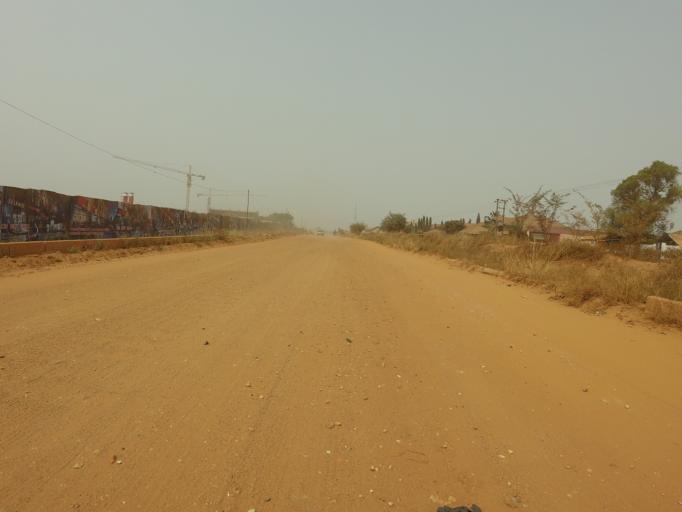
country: GH
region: Greater Accra
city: Medina Estates
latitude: 5.6321
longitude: -0.1245
